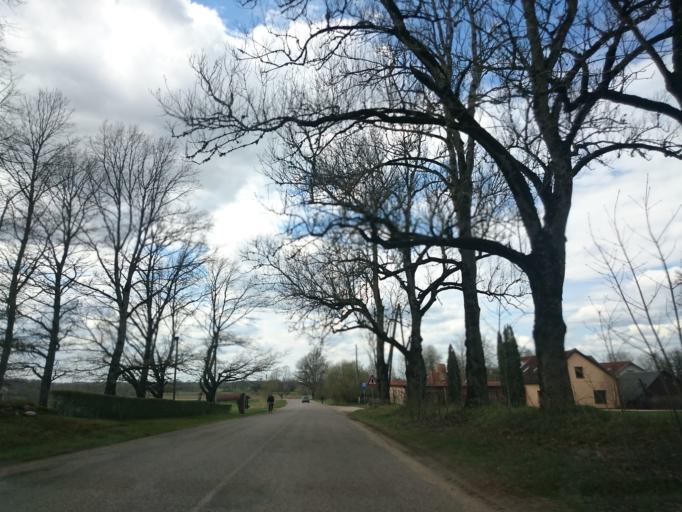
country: LV
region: Talsu Rajons
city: Sabile
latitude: 56.9490
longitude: 22.3696
